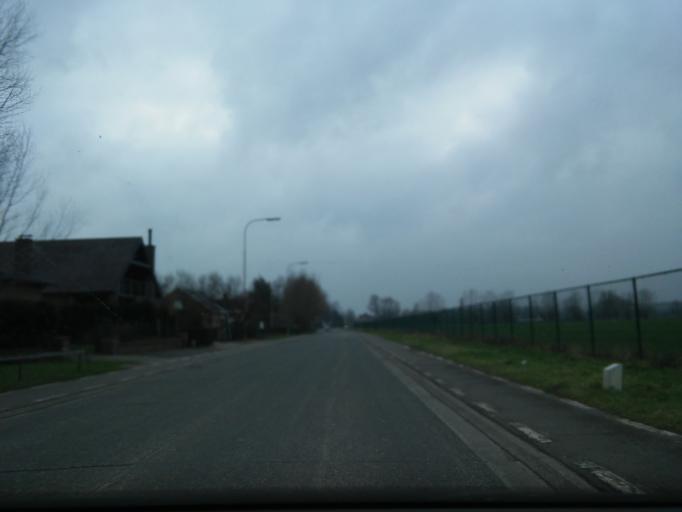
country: BE
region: Flanders
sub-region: Provincie Oost-Vlaanderen
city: Wetteren
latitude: 51.0325
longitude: 3.8920
